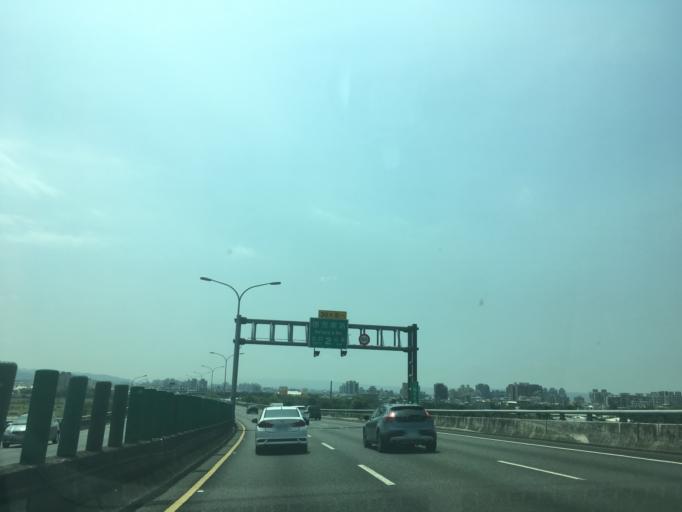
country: TW
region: Taiwan
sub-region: Taichung City
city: Taichung
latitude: 24.1218
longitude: 120.7014
